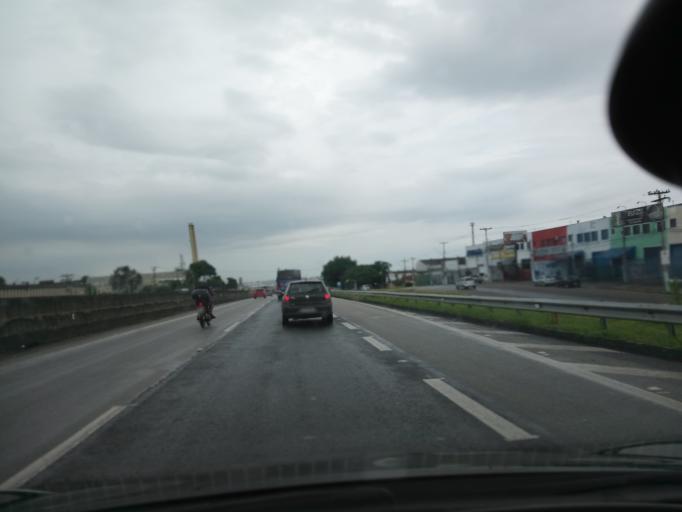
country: BR
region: Sao Paulo
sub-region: Campinas
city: Campinas
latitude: -22.9454
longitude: -47.0892
